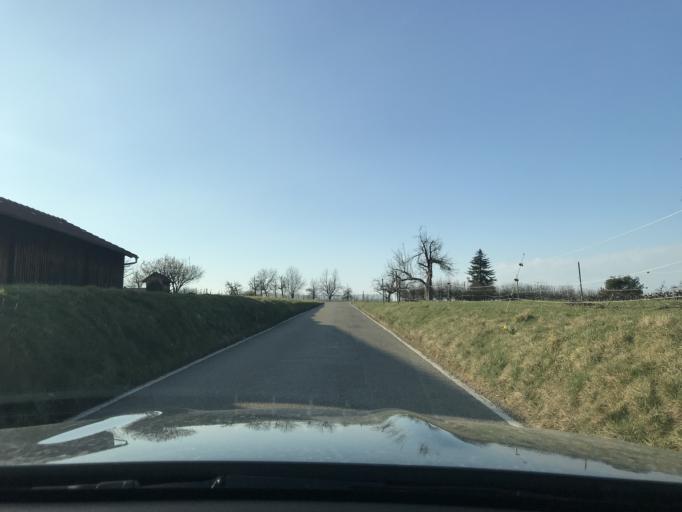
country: DE
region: Baden-Wuerttemberg
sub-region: Regierungsbezirk Stuttgart
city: Korb
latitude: 48.8302
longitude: 9.3704
